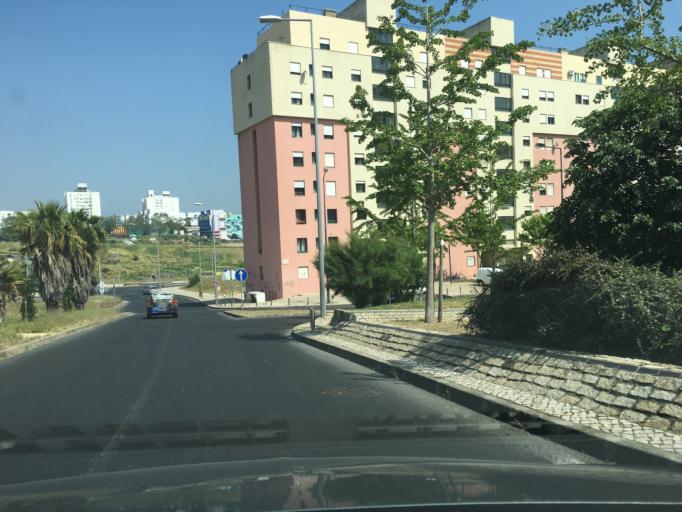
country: PT
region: Lisbon
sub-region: Lisbon
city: Lisbon
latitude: 38.7473
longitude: -9.1197
